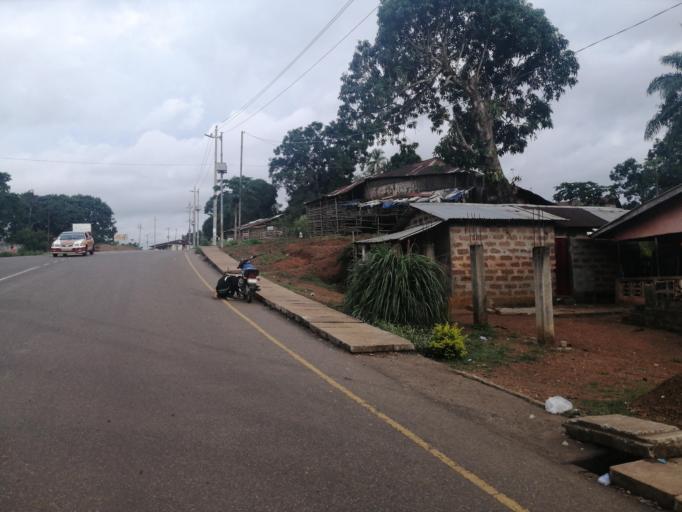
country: SL
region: Northern Province
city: Port Loko
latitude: 8.7691
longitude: -12.7872
